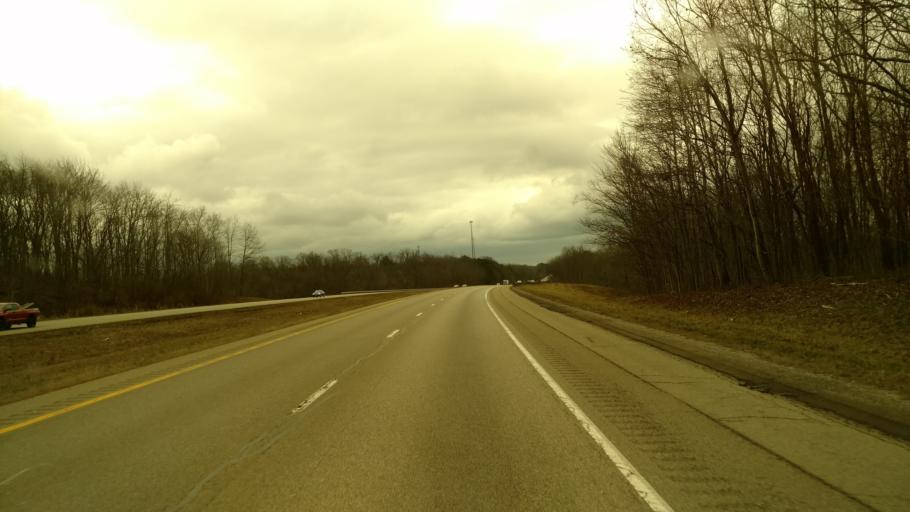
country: US
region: Ohio
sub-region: Muskingum County
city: Zanesville
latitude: 39.9447
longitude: -82.0845
